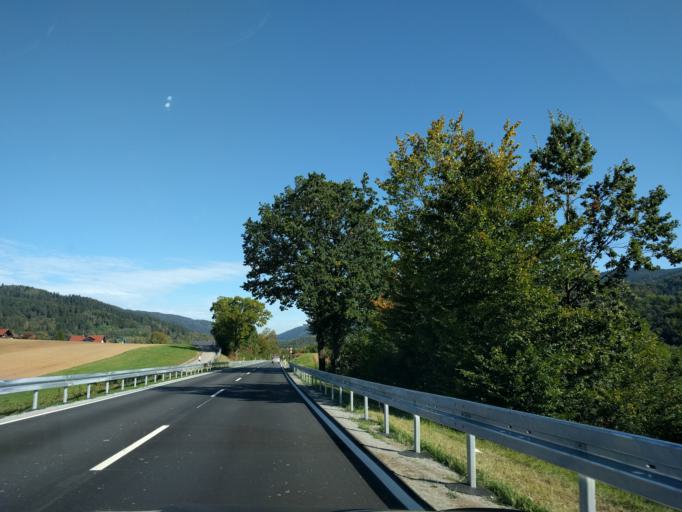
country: DE
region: Bavaria
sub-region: Lower Bavaria
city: Deggendorf
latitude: 48.8691
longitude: 12.9584
